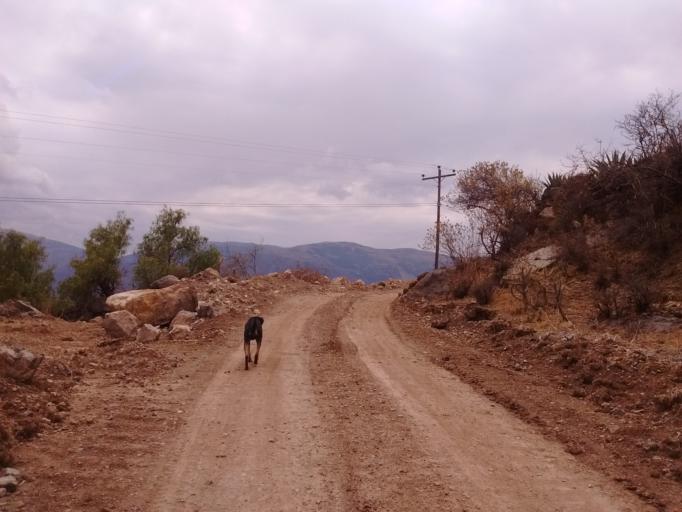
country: PE
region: Ayacucho
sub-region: Provincia de Victor Fajardo
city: Canaria
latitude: -13.8798
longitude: -73.9369
